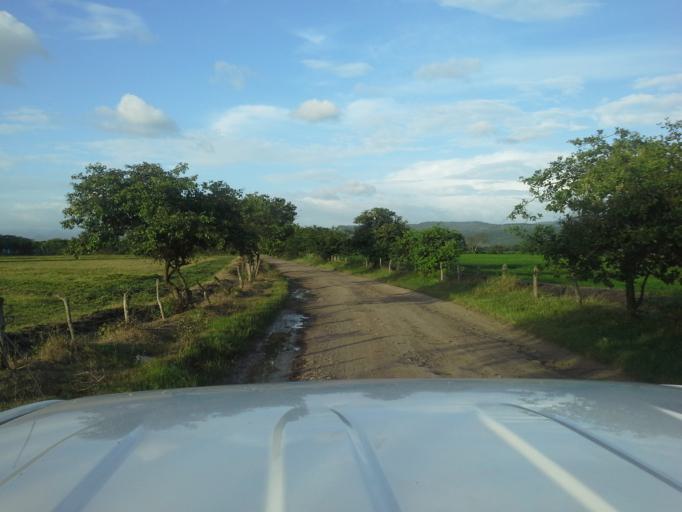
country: NI
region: Matagalpa
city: Ciudad Dario
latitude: 12.8024
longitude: -86.1399
